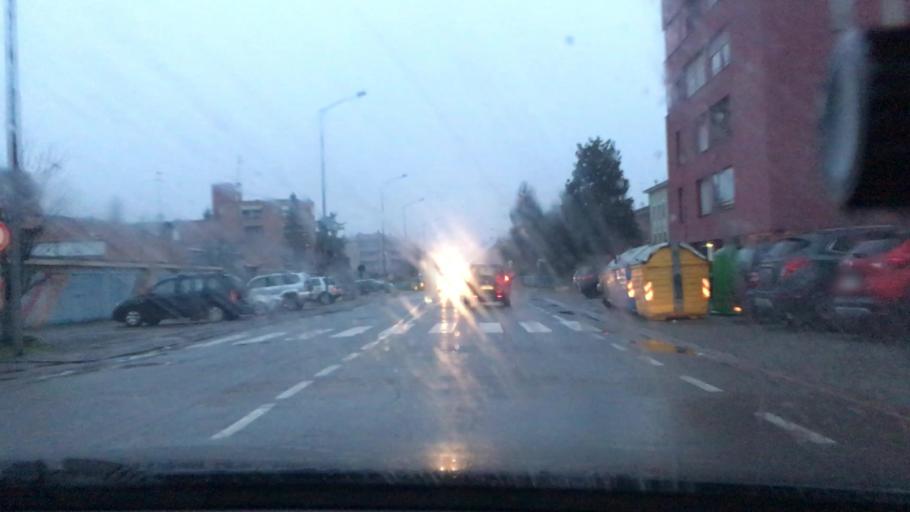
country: IT
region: Emilia-Romagna
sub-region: Provincia di Modena
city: Modena
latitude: 44.6400
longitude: 10.8886
